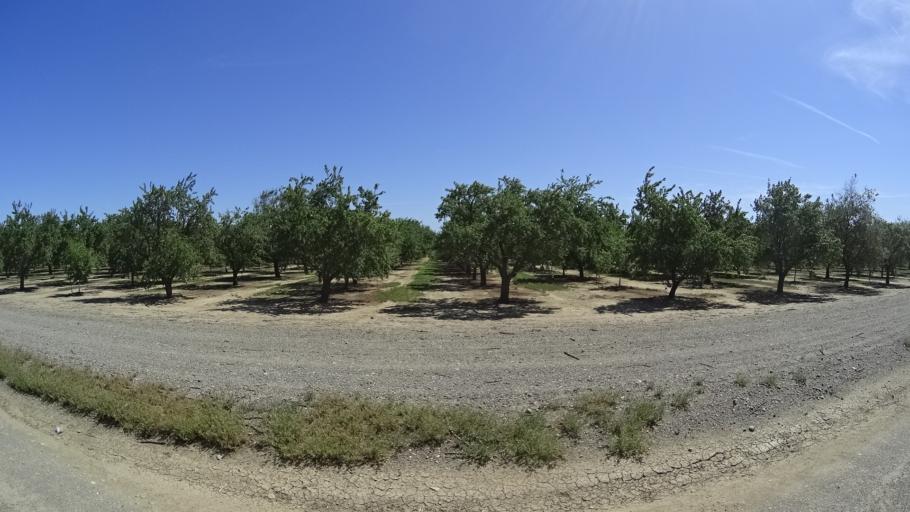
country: US
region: California
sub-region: Glenn County
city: Orland
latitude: 39.6699
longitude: -122.1782
